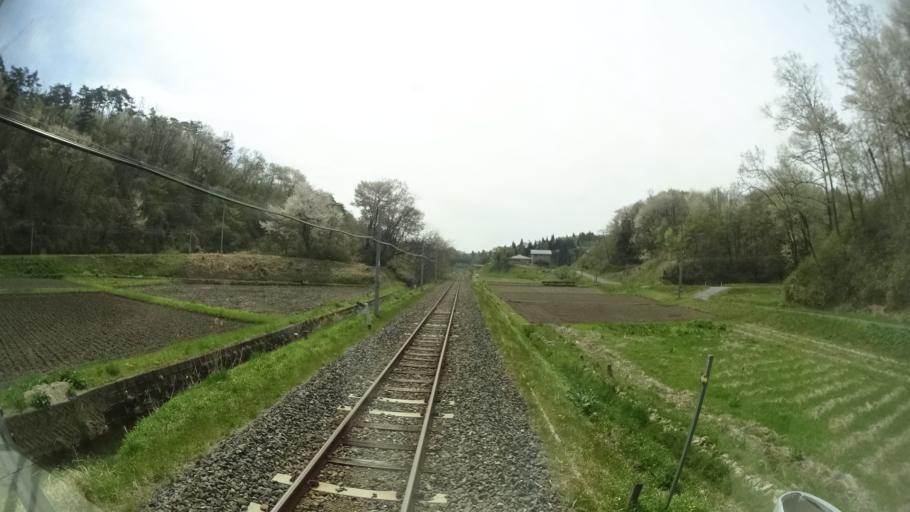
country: JP
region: Iwate
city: Ichinoseki
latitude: 38.9478
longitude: 141.3365
